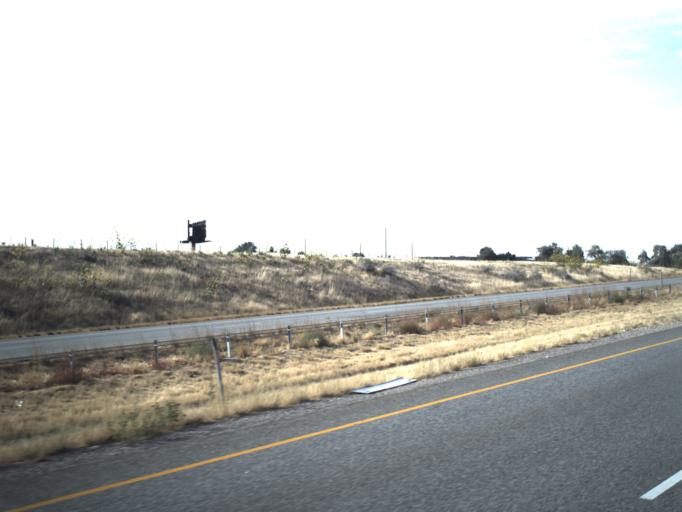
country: US
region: Utah
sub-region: Weber County
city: Riverdale
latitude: 41.1814
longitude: -112.0110
